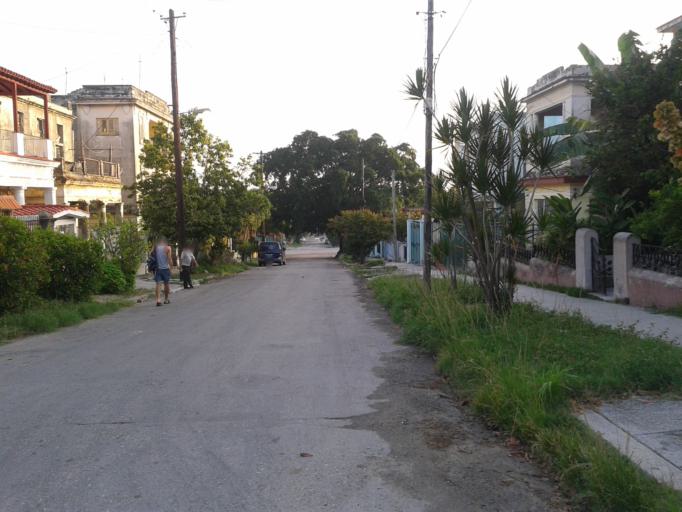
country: CU
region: La Habana
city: Diez de Octubre
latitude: 23.0936
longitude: -82.3708
